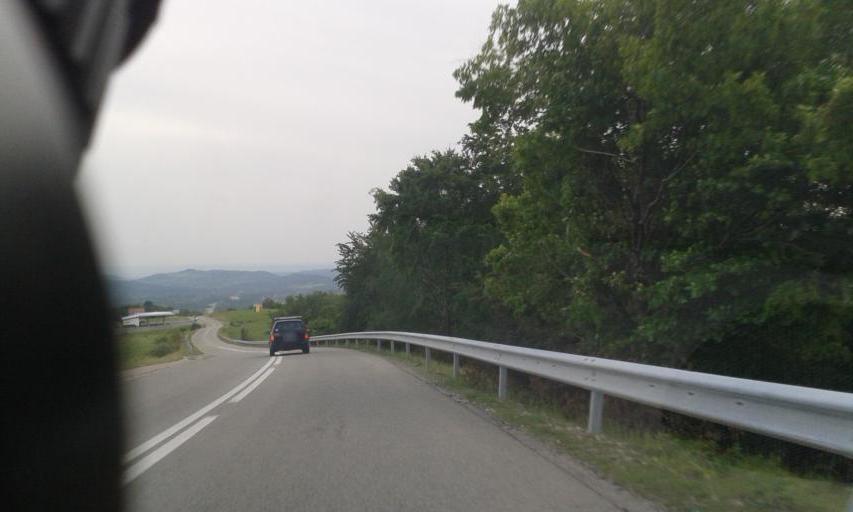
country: RO
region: Gorj
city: Novaci-Straini
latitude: 45.1997
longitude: 23.6906
